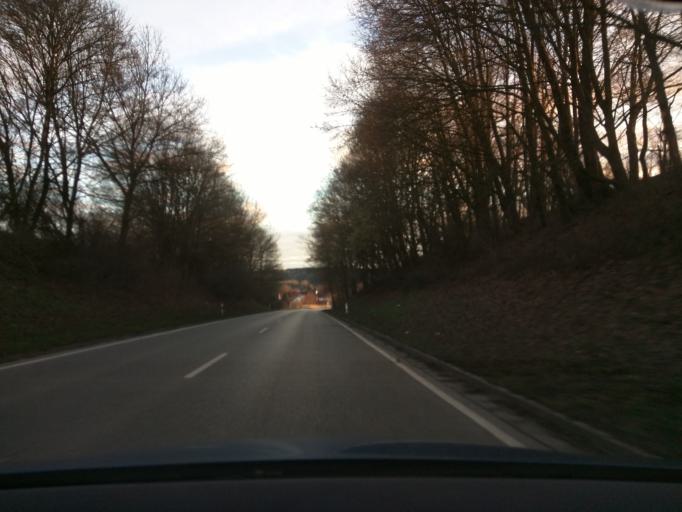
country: DE
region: Bavaria
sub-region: Upper Bavaria
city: Zolling
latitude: 48.4584
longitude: 11.7683
